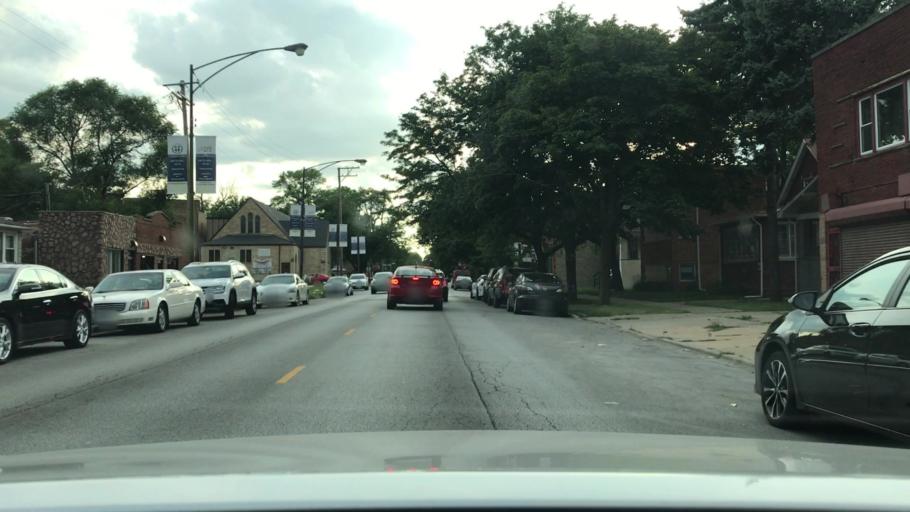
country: US
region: Illinois
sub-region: Cook County
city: Evergreen Park
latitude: 41.7141
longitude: -87.6559
